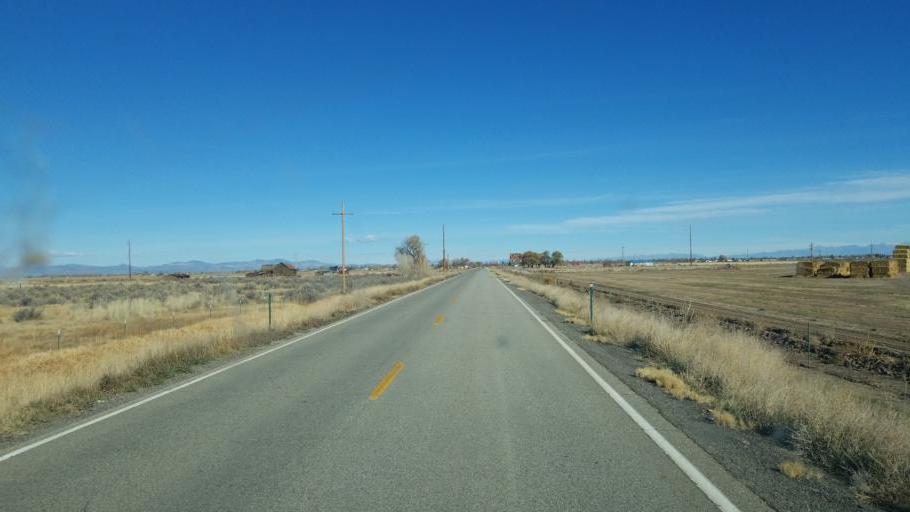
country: US
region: Colorado
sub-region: Rio Grande County
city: Monte Vista
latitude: 37.5429
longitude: -106.1494
